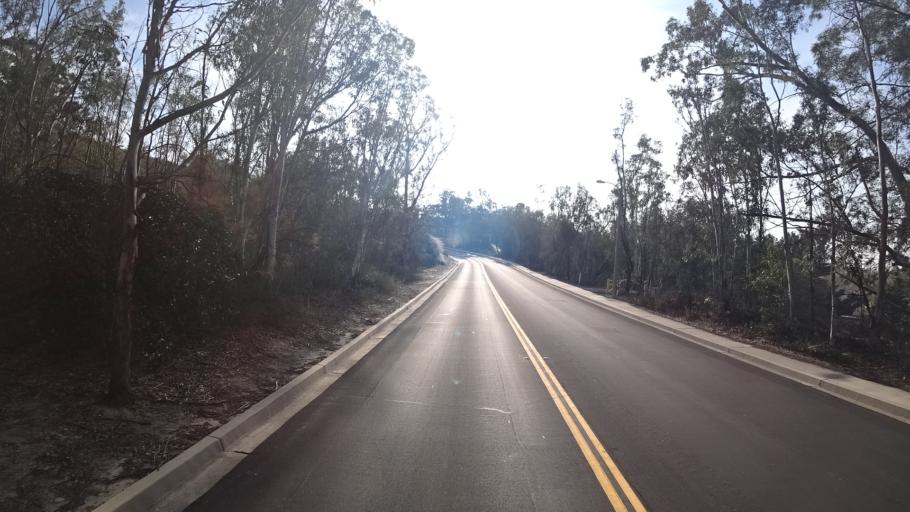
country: US
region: California
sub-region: Orange County
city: Lake Forest
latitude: 33.6509
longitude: -117.6814
